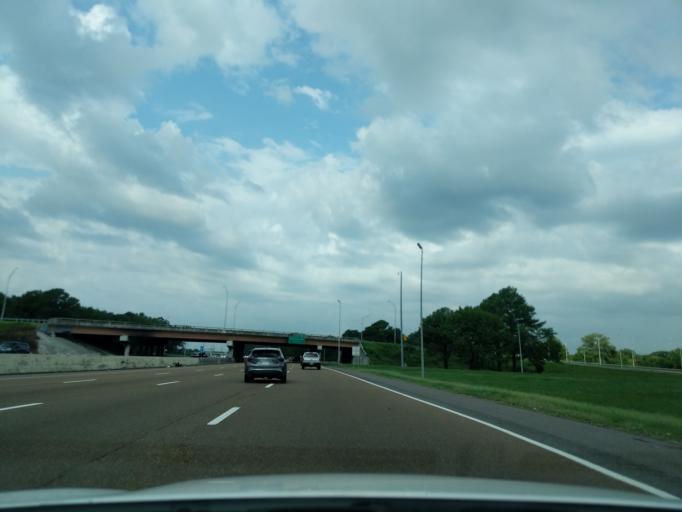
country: US
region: Tennessee
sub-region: Shelby County
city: Germantown
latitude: 35.0839
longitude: -89.8913
